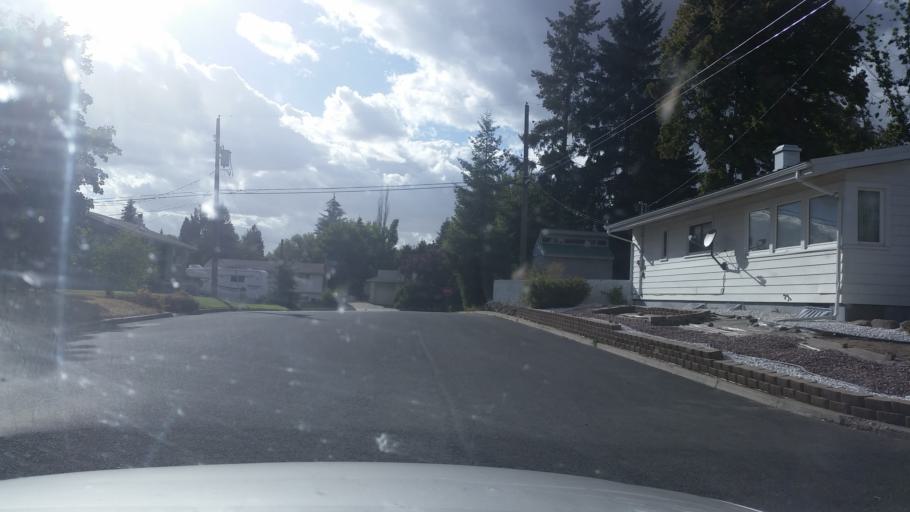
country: US
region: Washington
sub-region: Spokane County
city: Cheney
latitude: 47.4834
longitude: -117.5910
